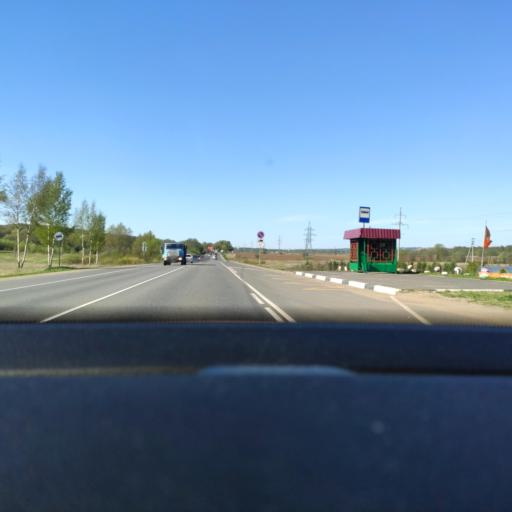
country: RU
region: Moskovskaya
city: Yakhroma
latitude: 56.3177
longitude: 37.4809
